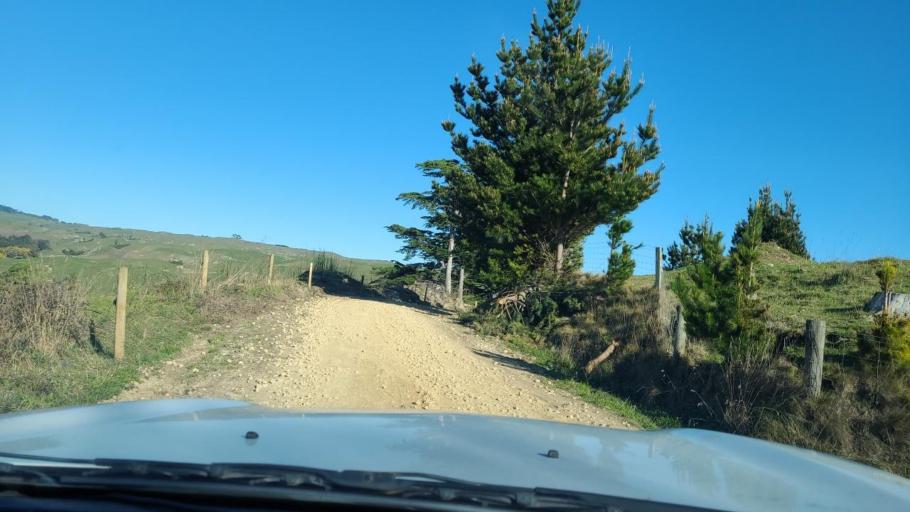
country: NZ
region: Hawke's Bay
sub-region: Hastings District
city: Hastings
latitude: -39.7932
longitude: 176.9718
